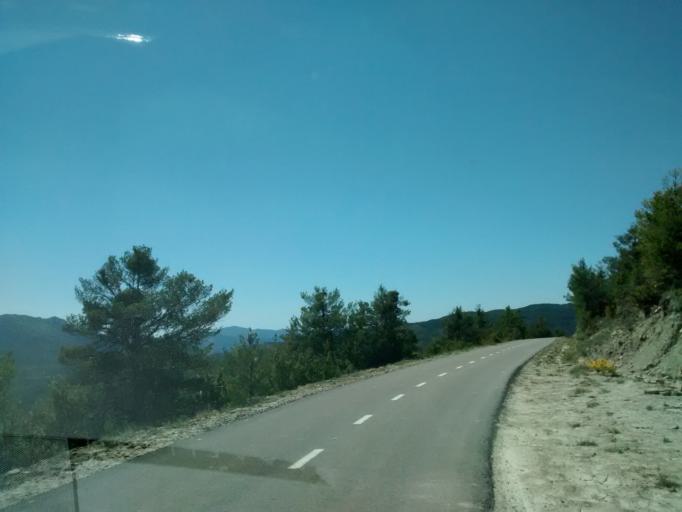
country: ES
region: Aragon
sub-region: Provincia de Huesca
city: Borau
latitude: 42.6690
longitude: -0.6039
